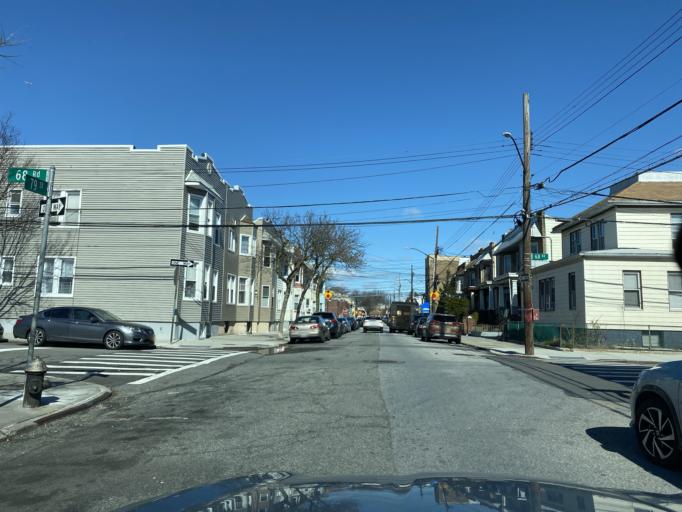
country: US
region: New York
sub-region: Kings County
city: East New York
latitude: 40.7103
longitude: -73.8734
